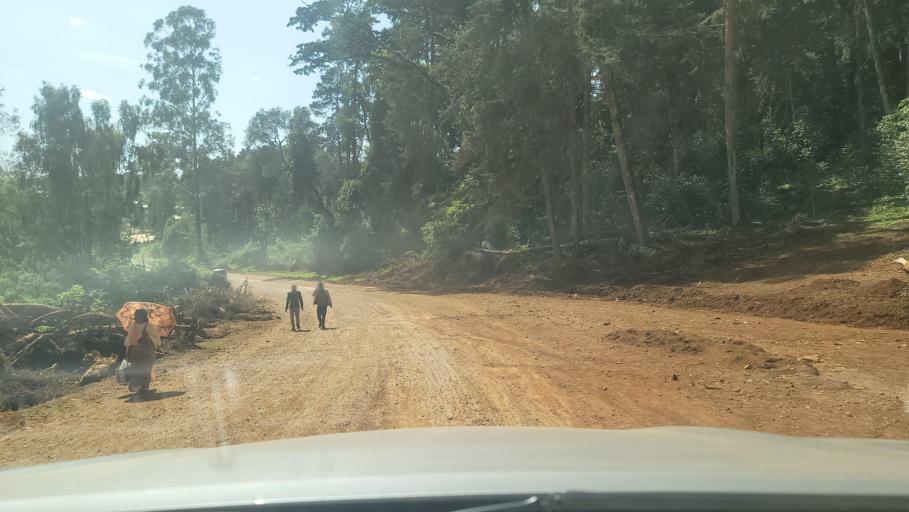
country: ET
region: Oromiya
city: Agaro
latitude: 7.7860
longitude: 36.4263
